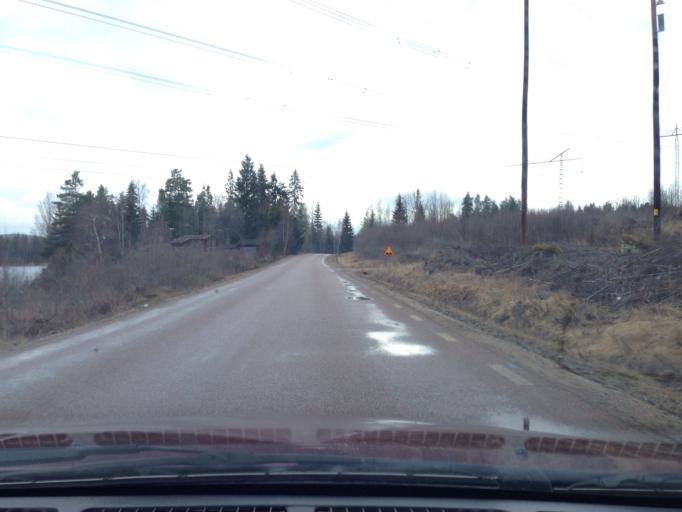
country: SE
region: Dalarna
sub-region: Ludvika Kommun
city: Ludvika
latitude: 60.1612
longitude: 15.2566
